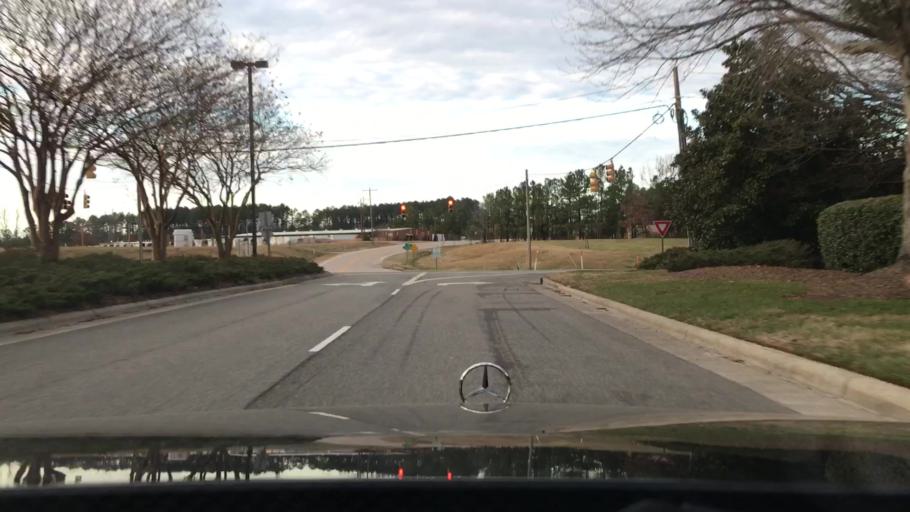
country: US
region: North Carolina
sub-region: Wake County
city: Morrisville
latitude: 35.8977
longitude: -78.7712
